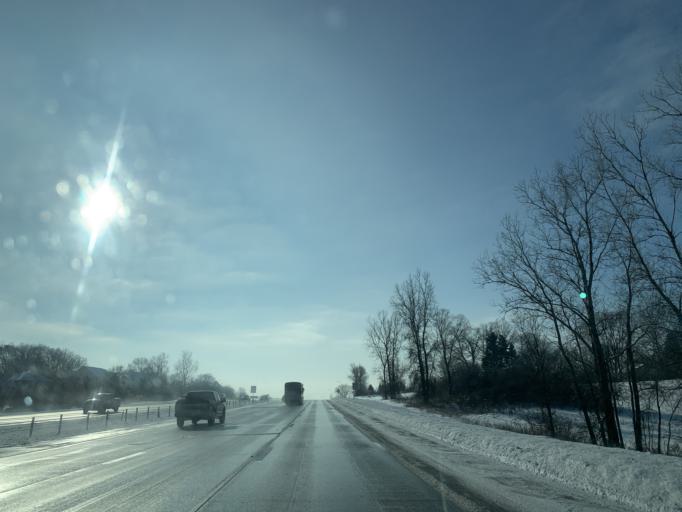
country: US
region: Minnesota
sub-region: Dakota County
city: Apple Valley
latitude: 44.7583
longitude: -93.2181
